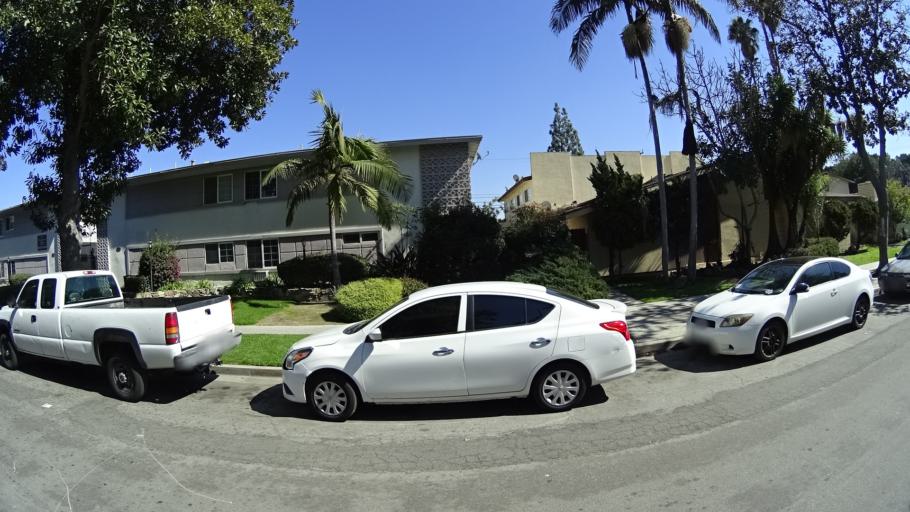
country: US
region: California
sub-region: Orange County
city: Anaheim
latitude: 33.8167
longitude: -117.9376
